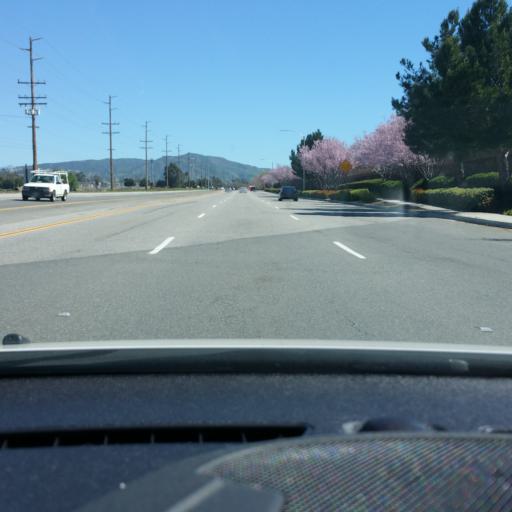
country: US
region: California
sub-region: Riverside County
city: Temecula
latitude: 33.4883
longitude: -117.0704
